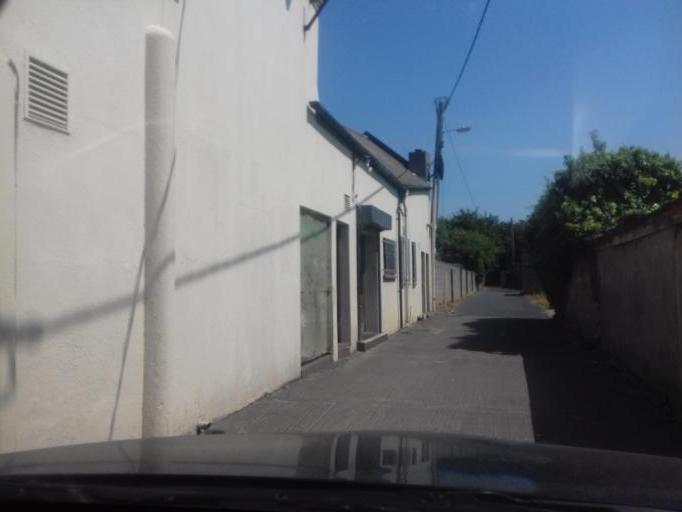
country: IE
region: Leinster
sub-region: Fingal County
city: Baldoyle
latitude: 53.3892
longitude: -6.1236
